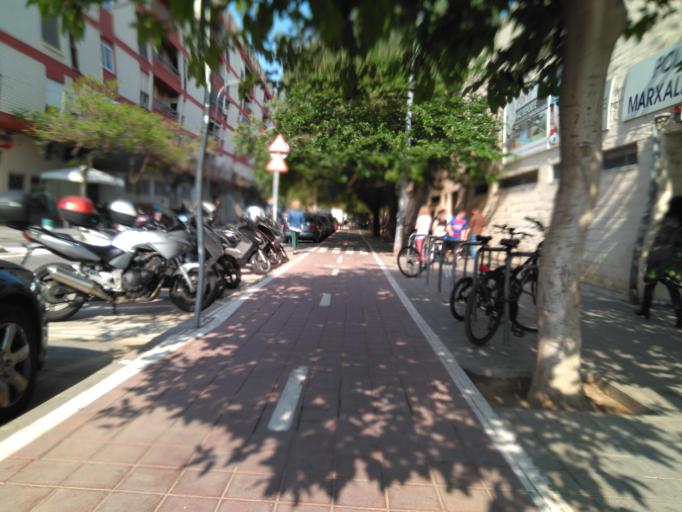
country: ES
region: Valencia
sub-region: Provincia de Valencia
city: Tavernes Blanques
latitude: 39.4887
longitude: -0.3814
